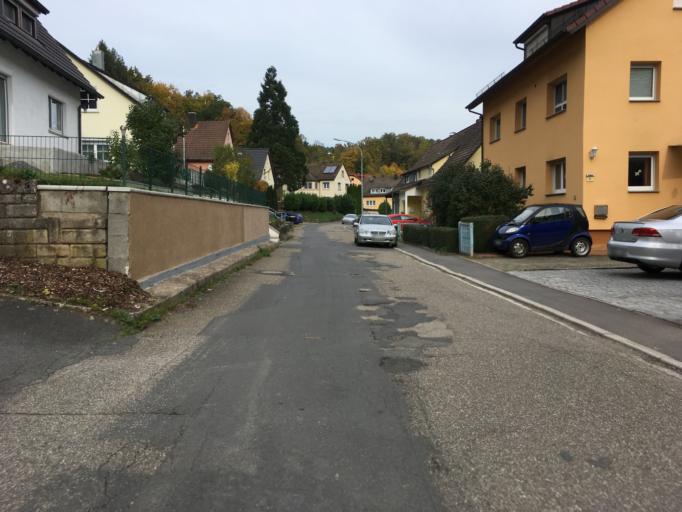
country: DE
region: Baden-Wuerttemberg
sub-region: Karlsruhe Region
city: Adelsheim
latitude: 49.4064
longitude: 9.3852
